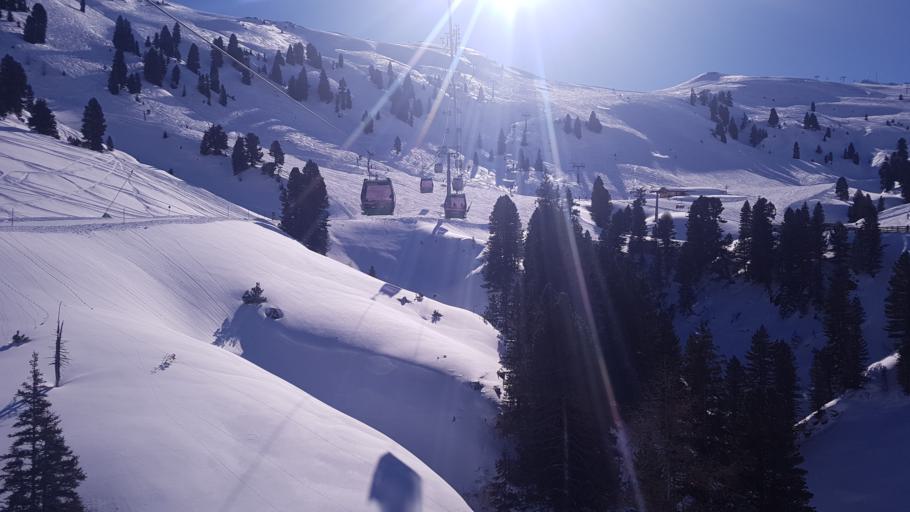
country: AT
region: Salzburg
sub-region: Politischer Bezirk Zell am See
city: Neukirchen am Grossvenediger
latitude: 47.2931
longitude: 12.2864
